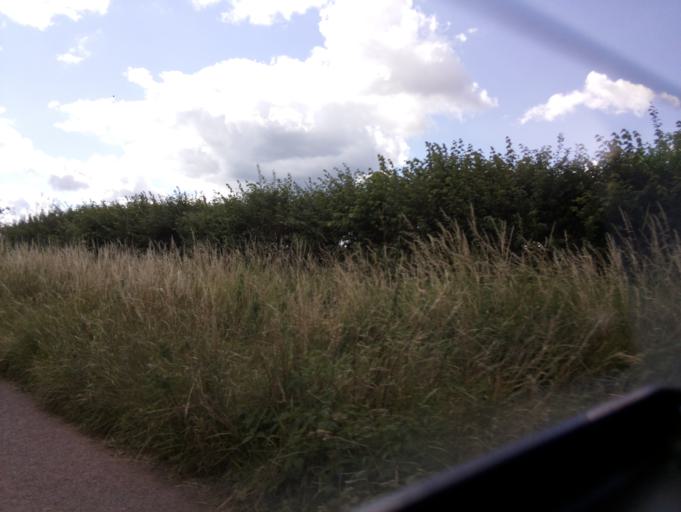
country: GB
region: England
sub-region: Gloucestershire
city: Newent
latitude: 51.8500
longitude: -2.3634
